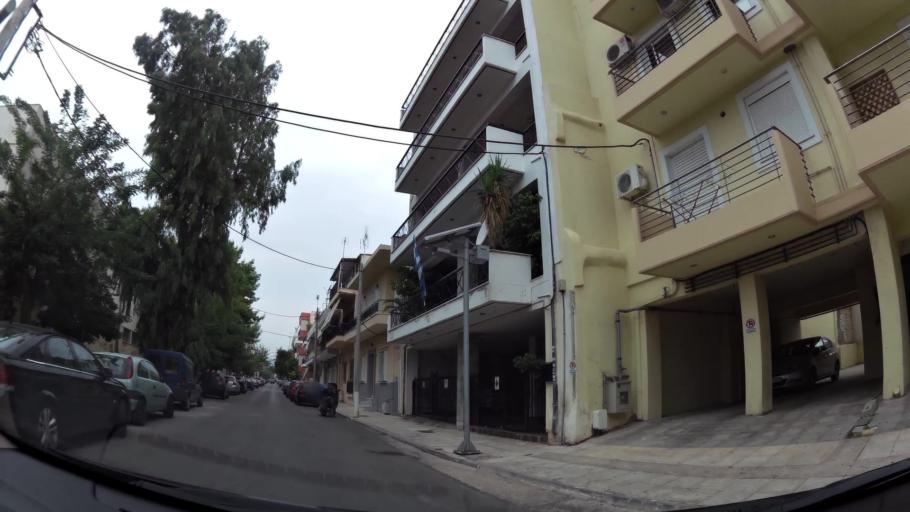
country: GR
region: Attica
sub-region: Nomarchia Athinas
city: Aigaleo
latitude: 37.9940
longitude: 23.6902
